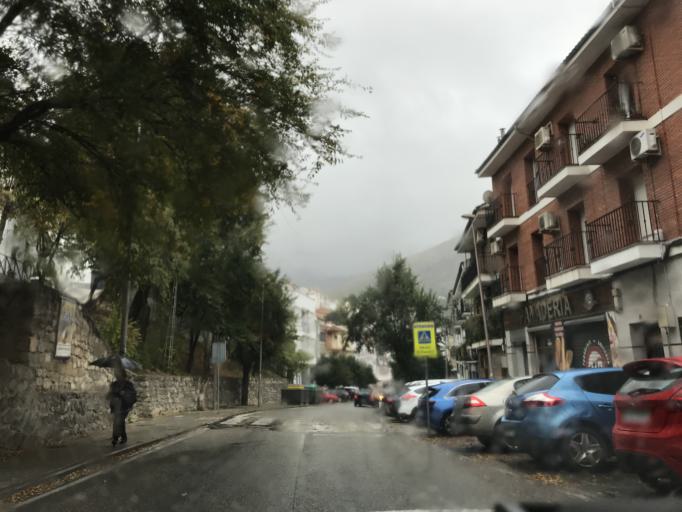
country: ES
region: Andalusia
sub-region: Provincia de Jaen
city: Cazorla
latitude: 37.9167
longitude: -3.0070
